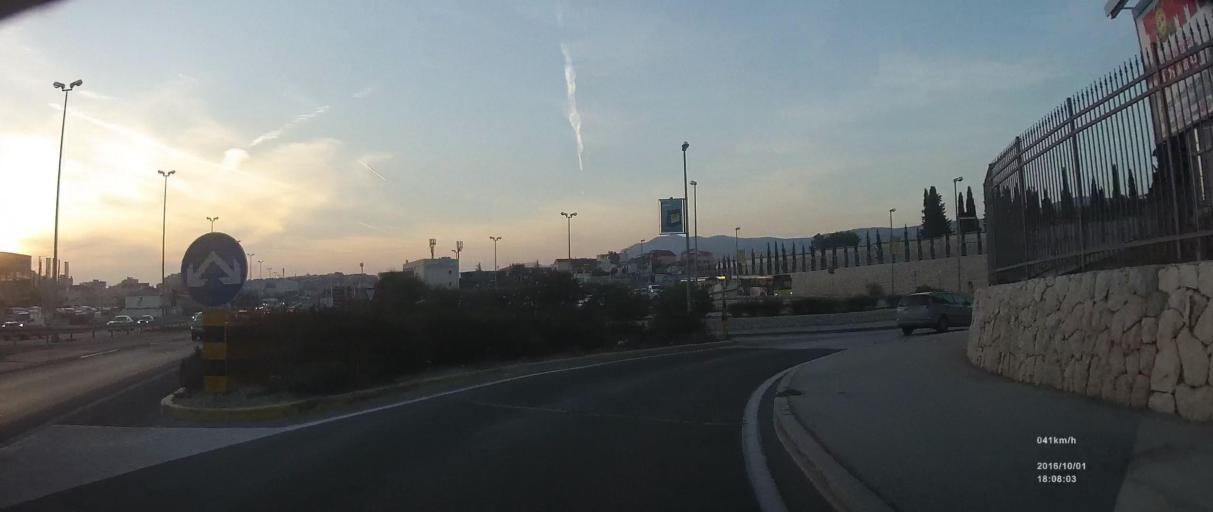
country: HR
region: Splitsko-Dalmatinska
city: Kamen
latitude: 43.5097
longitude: 16.4926
